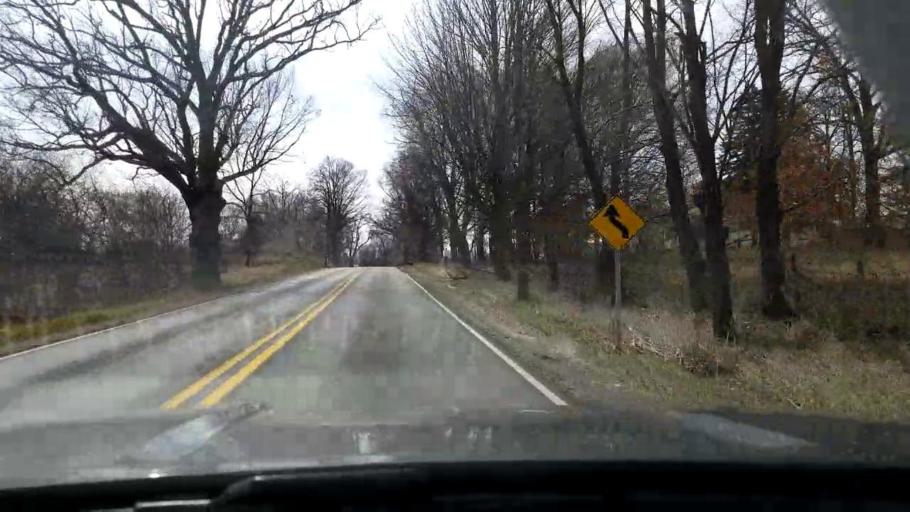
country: US
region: Michigan
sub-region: Jackson County
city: Spring Arbor
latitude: 42.1629
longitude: -84.5198
